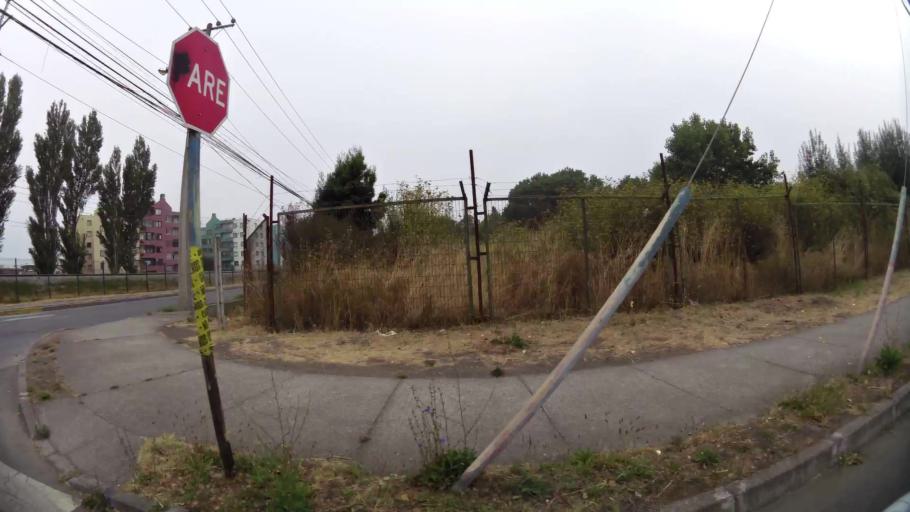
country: CL
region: Biobio
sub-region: Provincia de Concepcion
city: Concepcion
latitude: -36.7920
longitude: -73.0844
